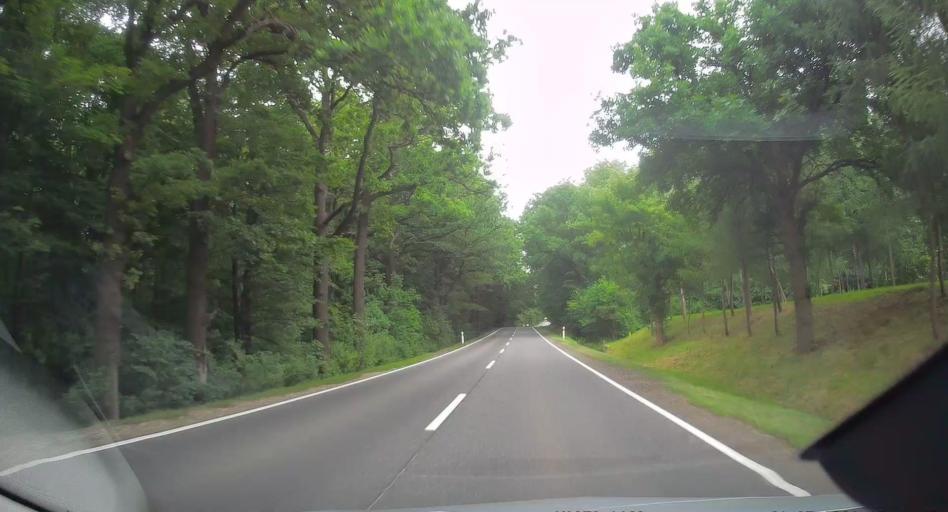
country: PL
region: Lower Silesian Voivodeship
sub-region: Powiat swidnicki
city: Swiebodzice
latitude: 50.8783
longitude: 16.2800
